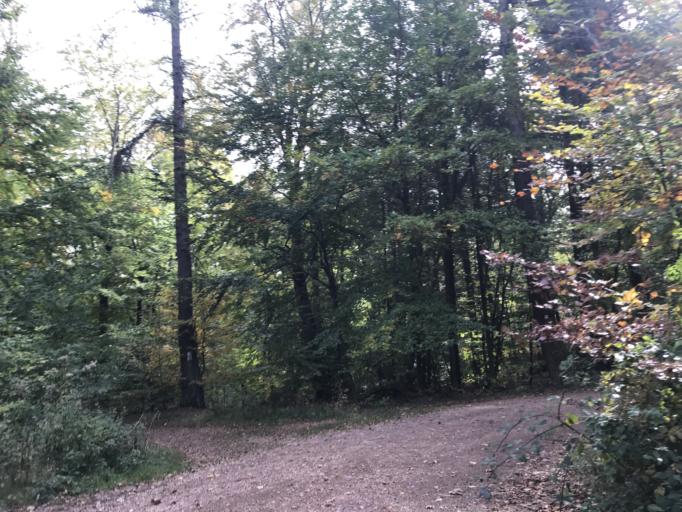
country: DE
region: Rheinland-Pfalz
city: Kirchheimbolanden
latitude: 49.6582
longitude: 7.9818
